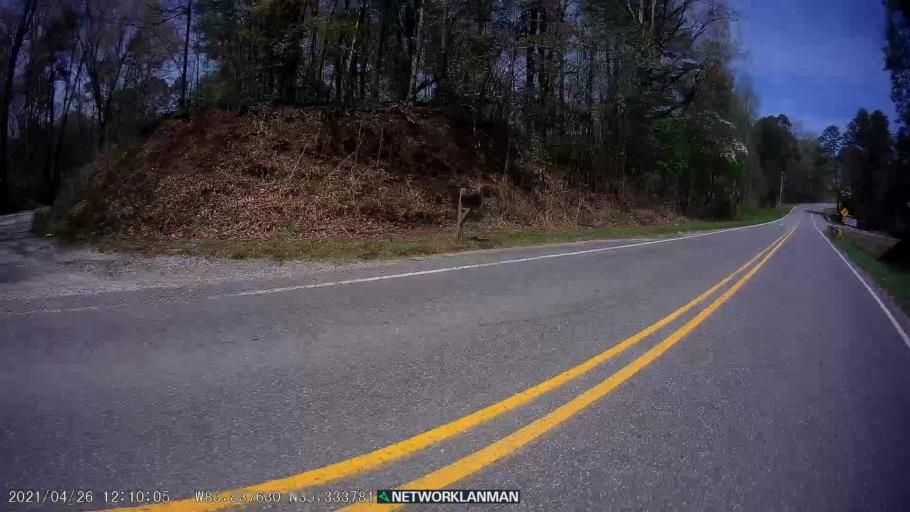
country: US
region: North Carolina
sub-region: Graham County
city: Robbinsville
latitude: 35.3339
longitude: -83.8372
